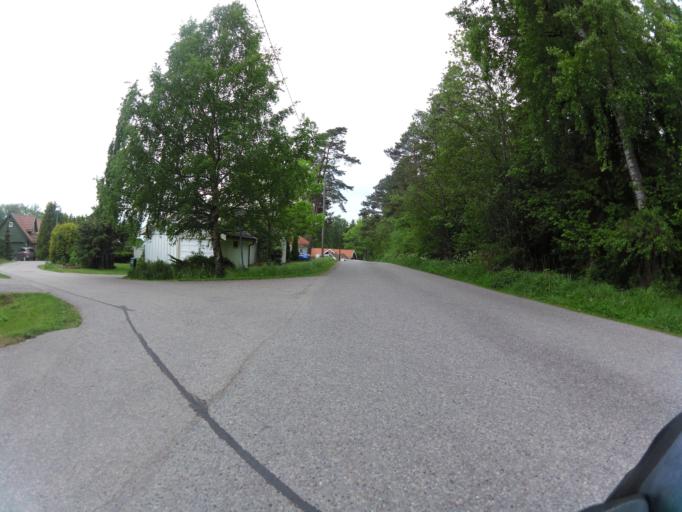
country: NO
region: Ostfold
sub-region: Moss
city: Moss
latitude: 59.3908
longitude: 10.6574
